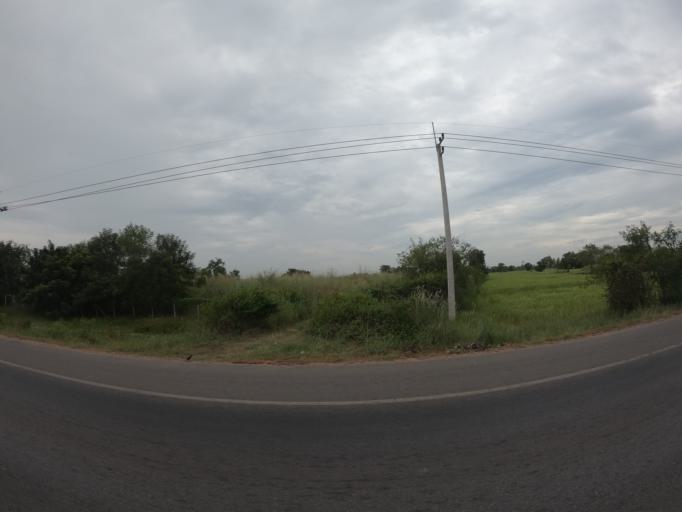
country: TH
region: Roi Et
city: Chiang Khwan
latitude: 16.1078
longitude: 103.8258
